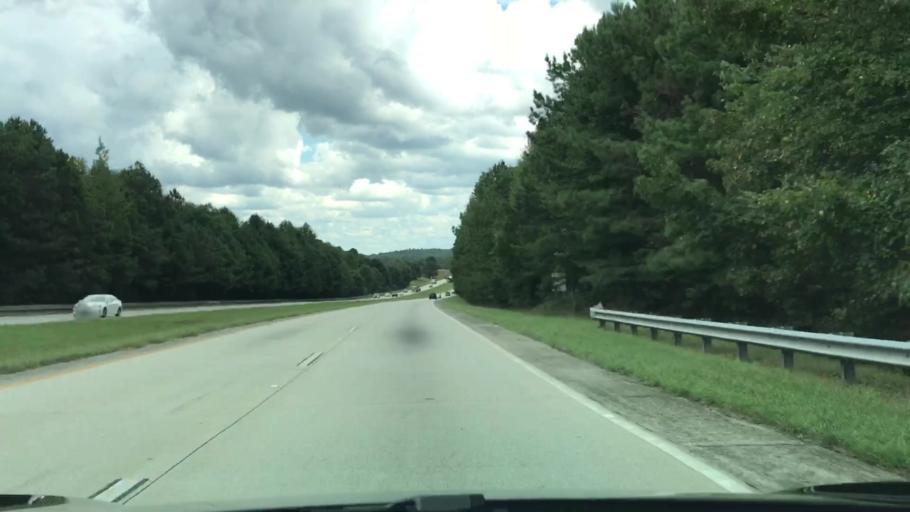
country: US
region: Georgia
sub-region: Barrow County
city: Statham
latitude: 33.9606
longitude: -83.6415
